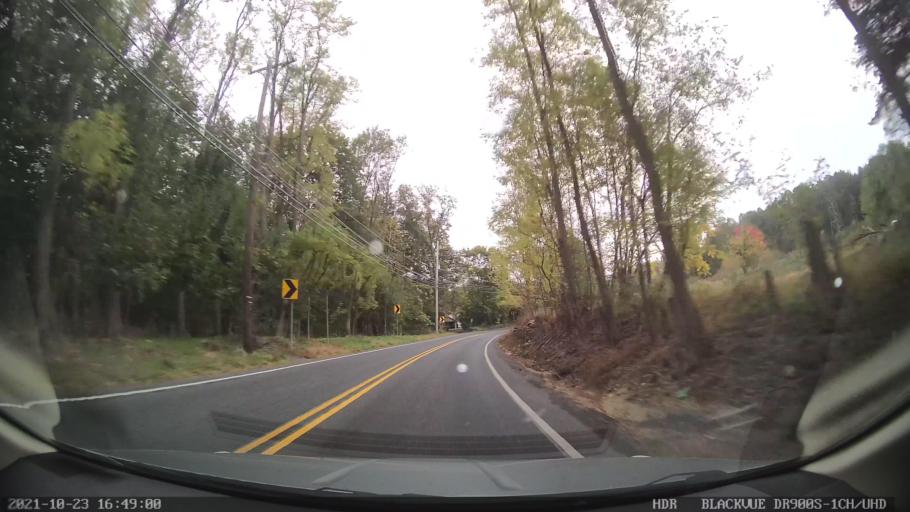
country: US
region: Pennsylvania
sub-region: Berks County
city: Red Lion
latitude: 40.4903
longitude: -75.6151
